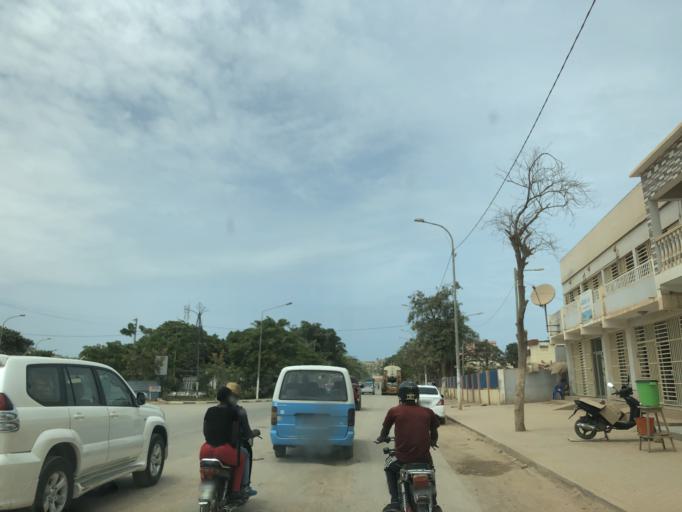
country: AO
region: Cuanza Sul
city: Sumbe
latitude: -11.2005
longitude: 13.8451
